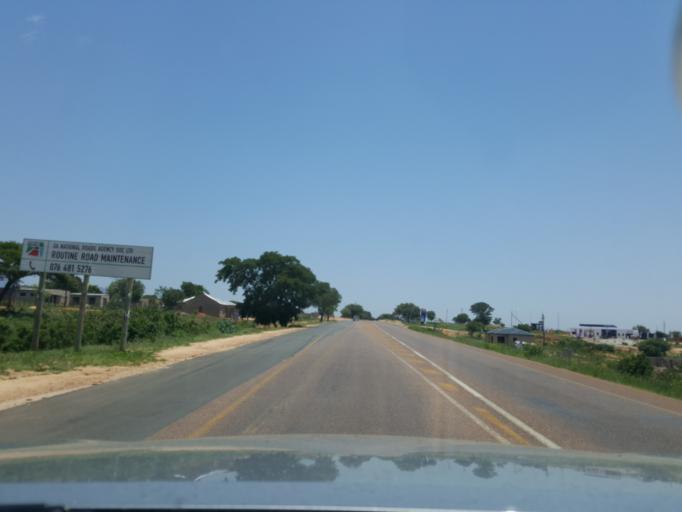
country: ZA
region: Limpopo
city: Thulamahashi
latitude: -24.6779
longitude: 31.0262
